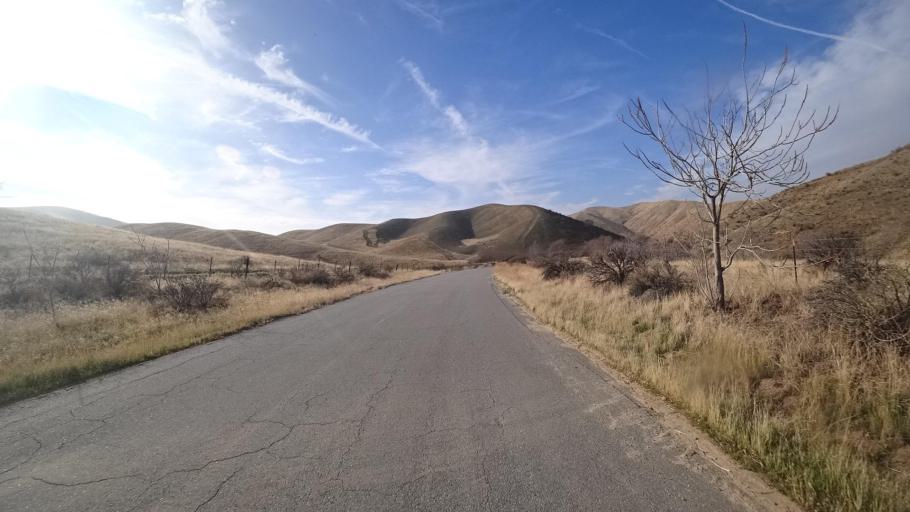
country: US
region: California
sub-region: Kern County
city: Bear Valley Springs
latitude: 35.2838
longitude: -118.6602
